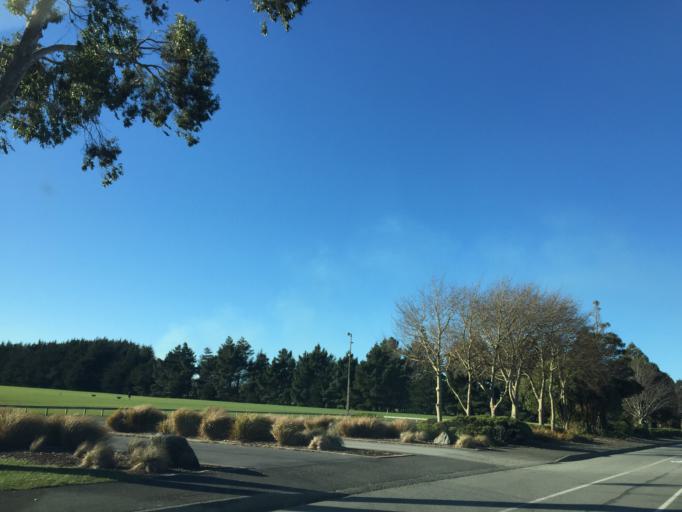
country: NZ
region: Southland
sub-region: Invercargill City
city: Invercargill
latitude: -46.3755
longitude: 168.3546
